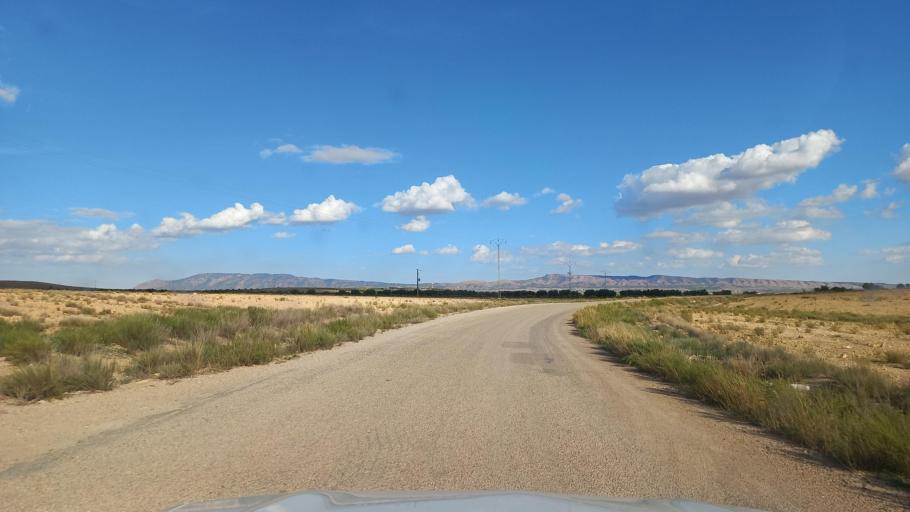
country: TN
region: Al Qasrayn
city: Sbiba
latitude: 35.3924
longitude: 9.0231
